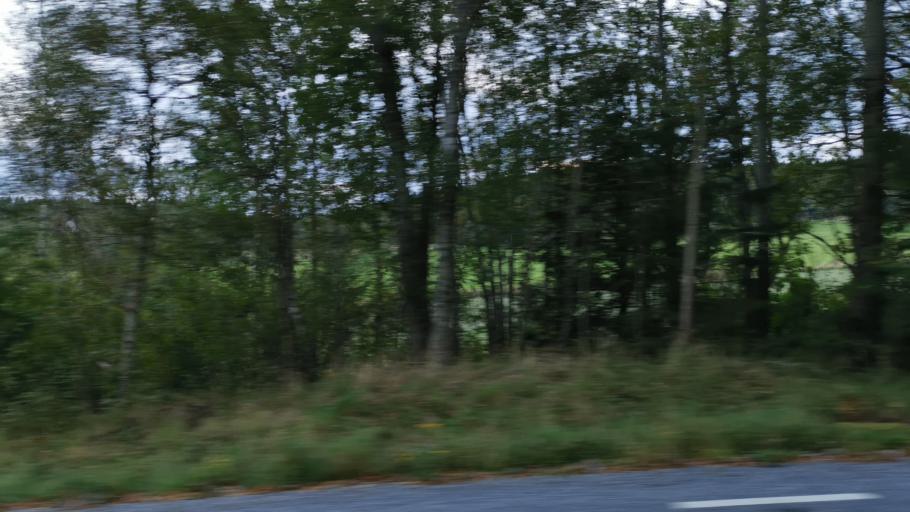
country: SE
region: Vaestra Goetaland
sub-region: Tanums Kommun
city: Tanumshede
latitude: 58.6834
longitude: 11.3367
